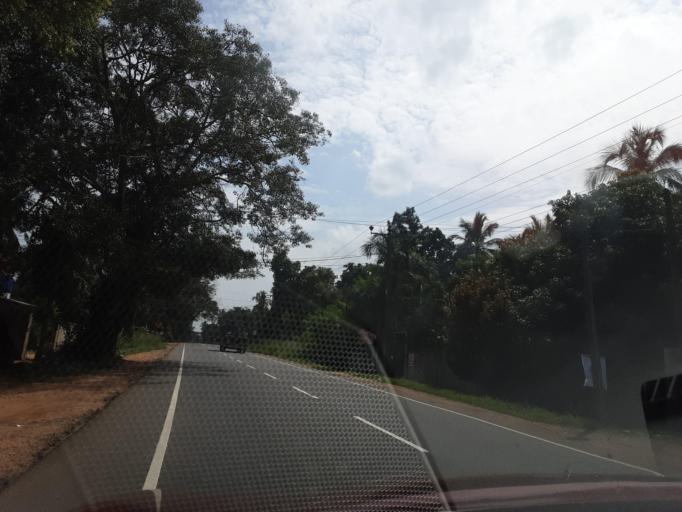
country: LK
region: Northern Province
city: Vavuniya
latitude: 8.5239
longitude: 80.5004
